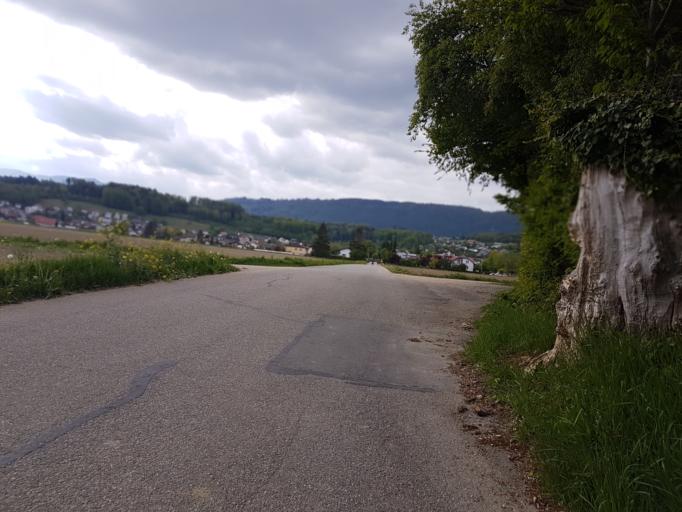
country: CH
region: Bern
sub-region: Biel/Bienne District
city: Meinisberg
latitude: 47.1440
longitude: 7.3311
